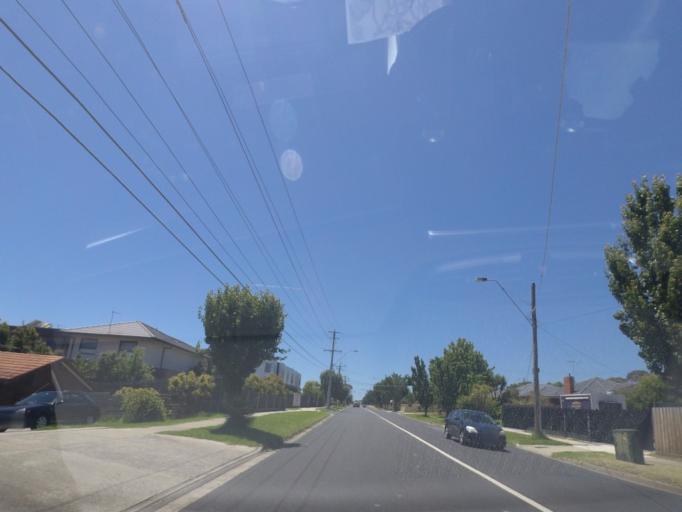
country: AU
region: Victoria
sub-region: Banyule
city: Bundoora
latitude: -37.6968
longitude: 145.0499
